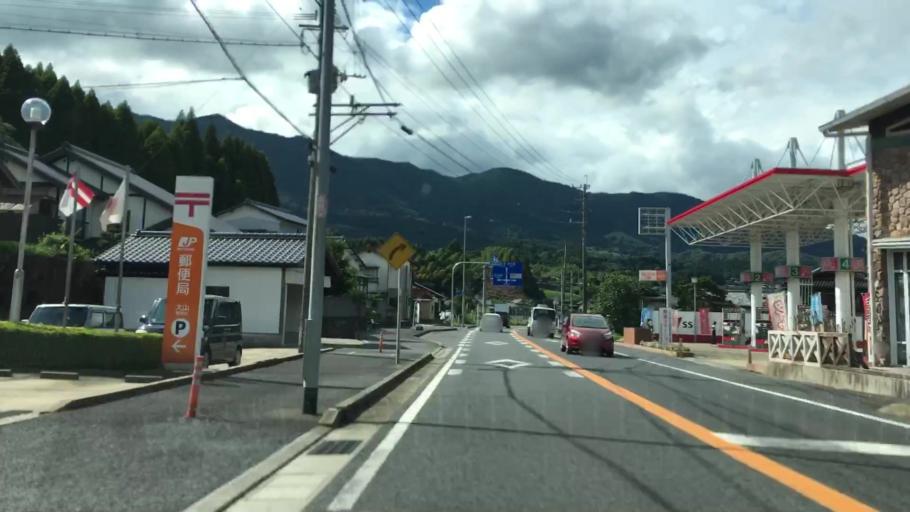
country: JP
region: Saga Prefecture
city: Imaricho-ko
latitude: 33.2226
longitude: 129.8488
